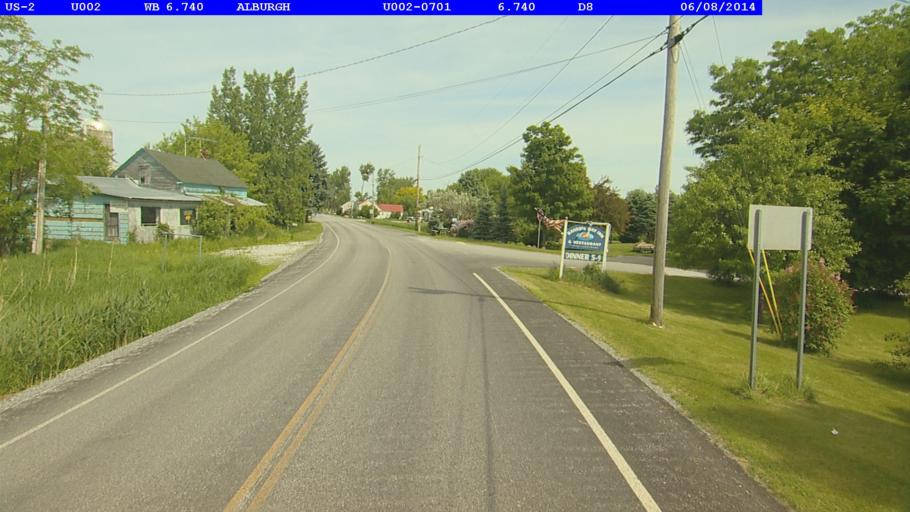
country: US
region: New York
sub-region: Clinton County
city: Rouses Point
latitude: 44.9538
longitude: -73.2709
